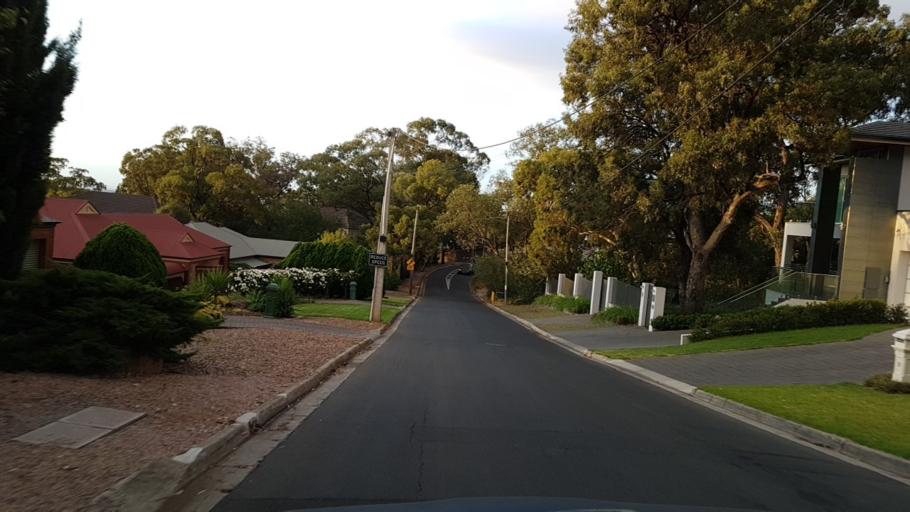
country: AU
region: South Australia
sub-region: Burnside
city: Hazelwood Park
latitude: -34.9416
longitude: 138.6683
